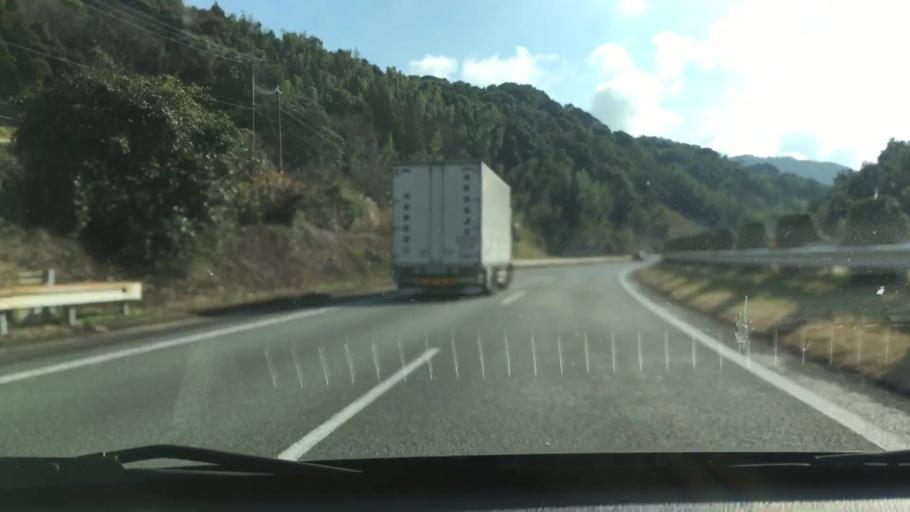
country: JP
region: Kumamoto
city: Matsubase
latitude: 32.6120
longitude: 130.7247
